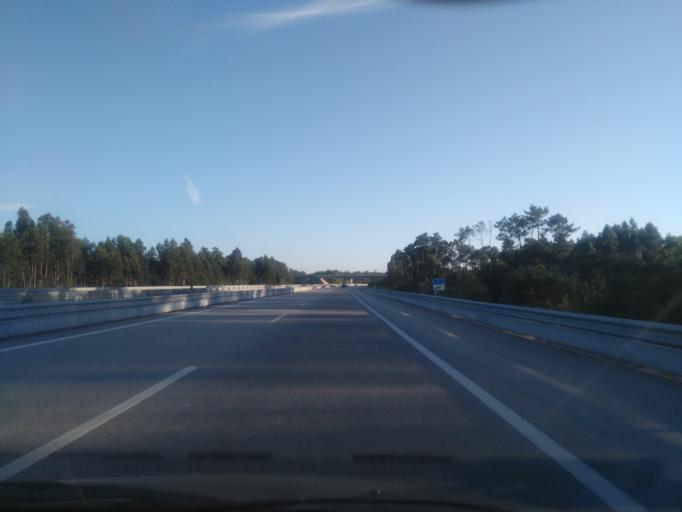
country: PT
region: Coimbra
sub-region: Figueira da Foz
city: Alhadas
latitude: 40.2391
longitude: -8.7845
